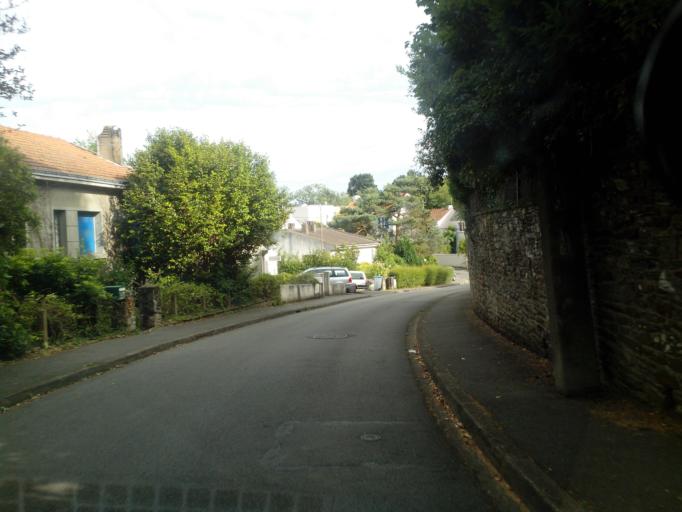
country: FR
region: Pays de la Loire
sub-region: Departement de la Loire-Atlantique
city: Nantes
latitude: 47.2516
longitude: -1.5793
